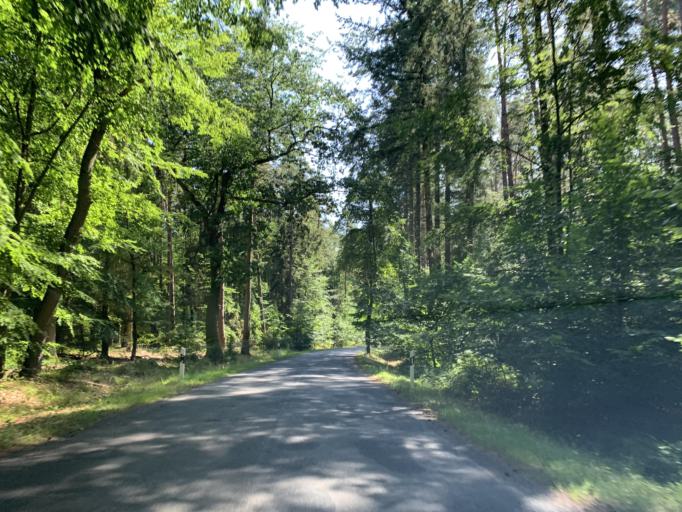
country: DE
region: Mecklenburg-Vorpommern
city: Carpin
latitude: 53.3393
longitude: 13.2421
